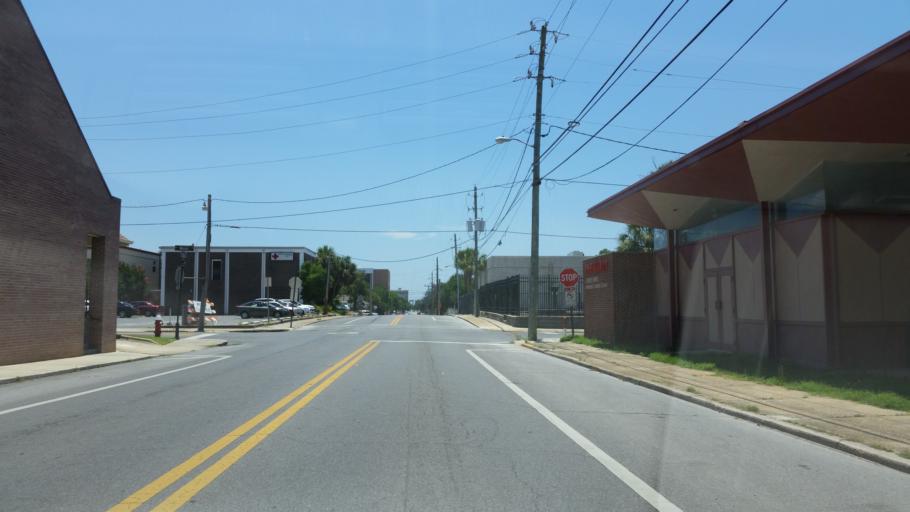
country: US
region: Florida
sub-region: Escambia County
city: Pensacola
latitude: 30.4167
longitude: -87.2178
